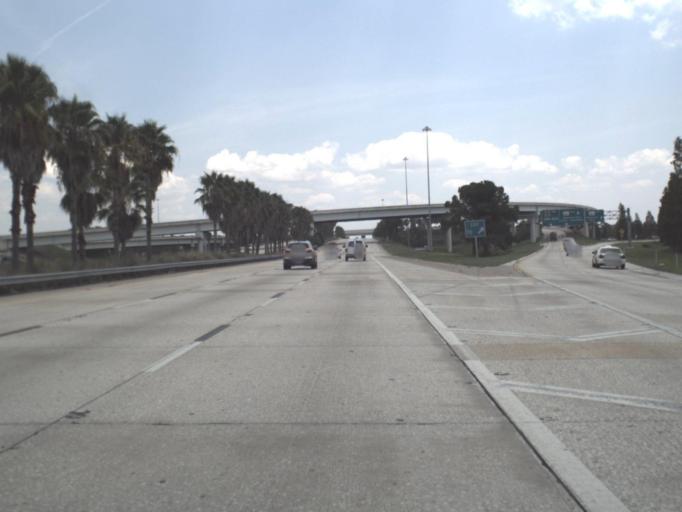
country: US
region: Florida
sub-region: Pinellas County
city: Feather Sound
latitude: 27.8750
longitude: -82.6623
